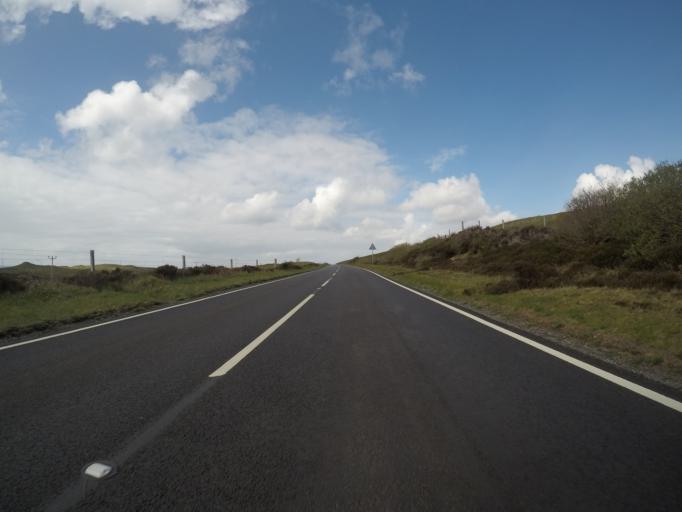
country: GB
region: Scotland
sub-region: Highland
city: Portree
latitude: 57.5371
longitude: -6.3617
